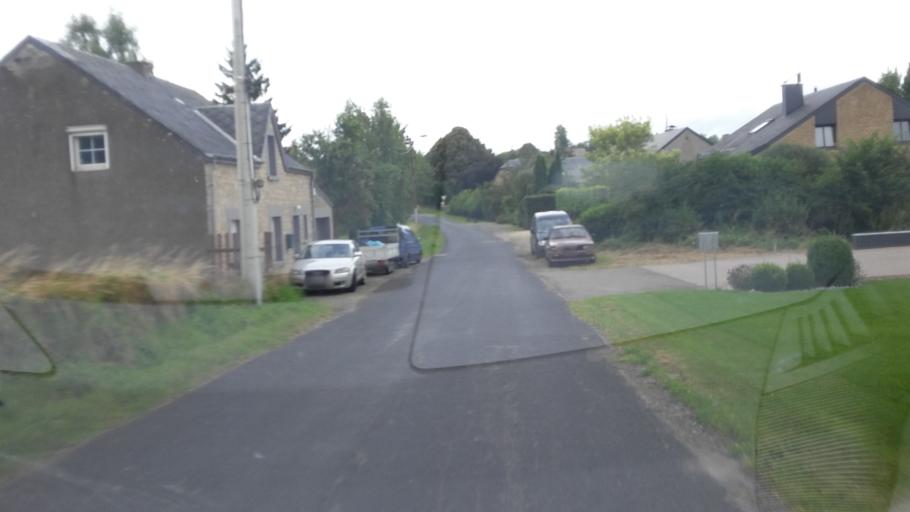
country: BE
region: Wallonia
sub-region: Province du Luxembourg
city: Arlon
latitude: 49.6903
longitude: 5.8397
